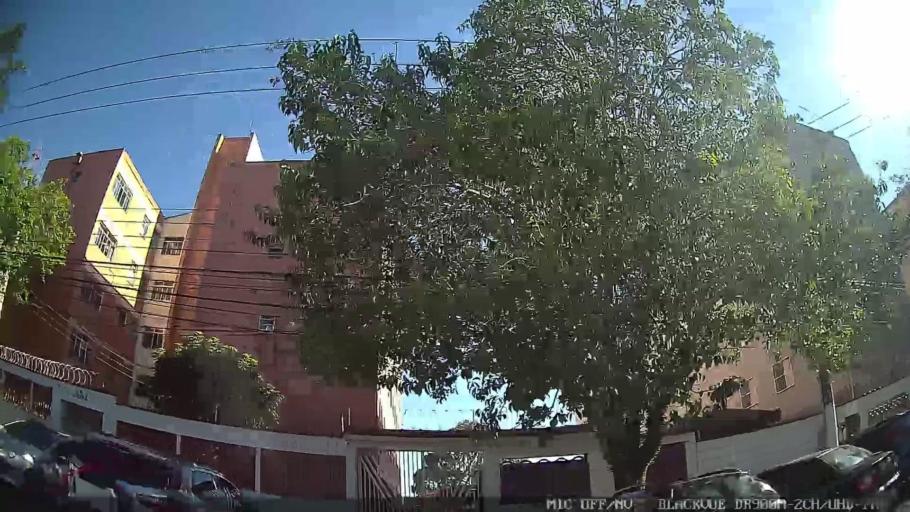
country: BR
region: Sao Paulo
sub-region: Sao Caetano Do Sul
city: Sao Caetano do Sul
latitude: -23.5496
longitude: -46.4843
